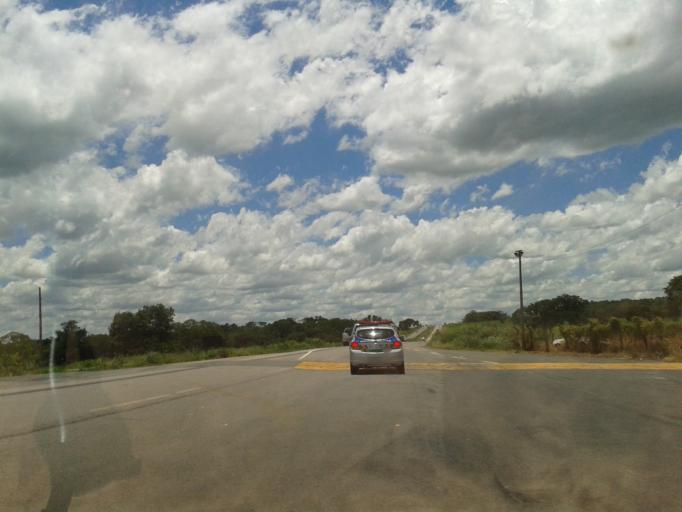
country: BR
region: Goias
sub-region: Jaragua
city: Jaragua
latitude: -15.9093
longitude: -49.2487
